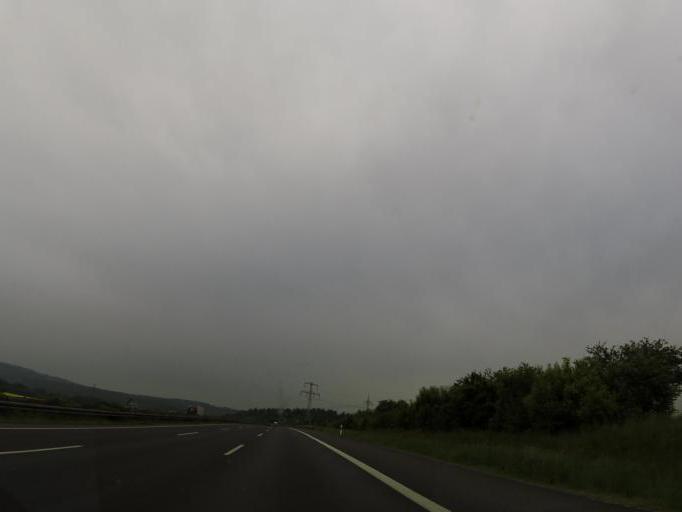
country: DE
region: Lower Saxony
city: Scheden
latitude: 51.4076
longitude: 9.7376
